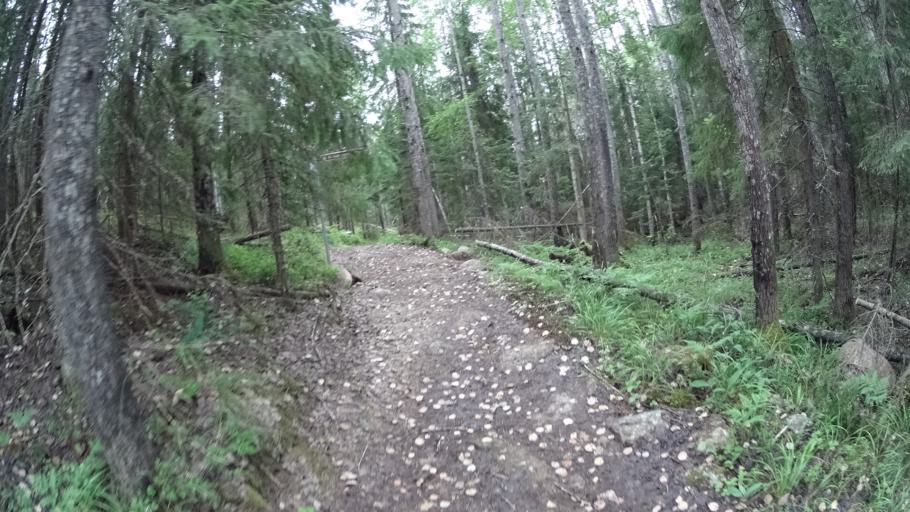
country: FI
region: Southern Savonia
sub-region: Mikkeli
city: Maentyharju
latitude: 61.1823
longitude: 26.8879
